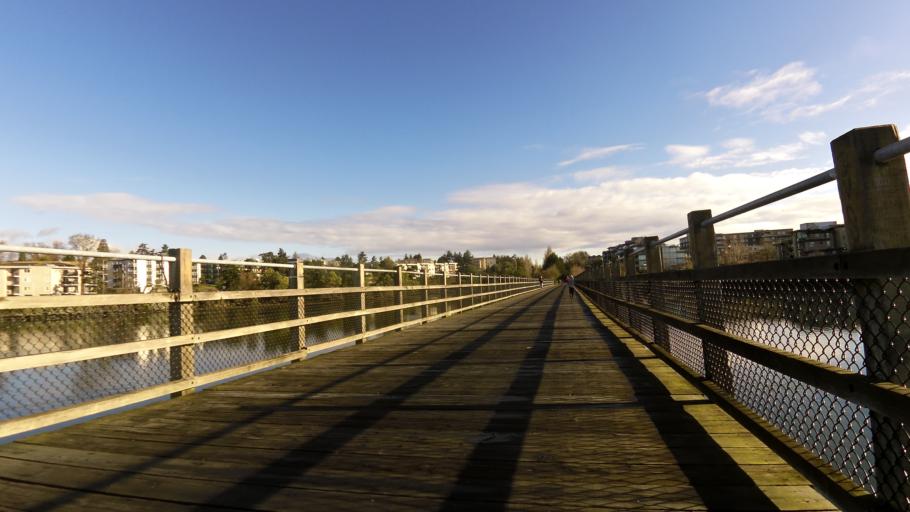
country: CA
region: British Columbia
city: Victoria
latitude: 48.4398
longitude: -123.3821
